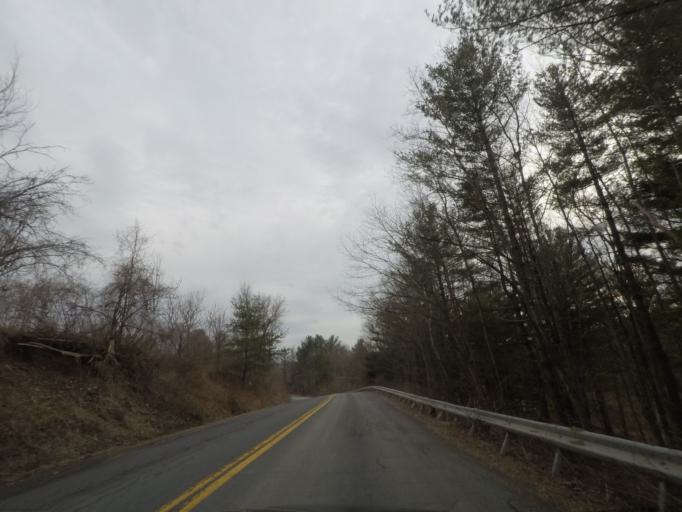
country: US
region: New York
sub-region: Rensselaer County
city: Hoosick Falls
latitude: 42.8668
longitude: -73.4504
